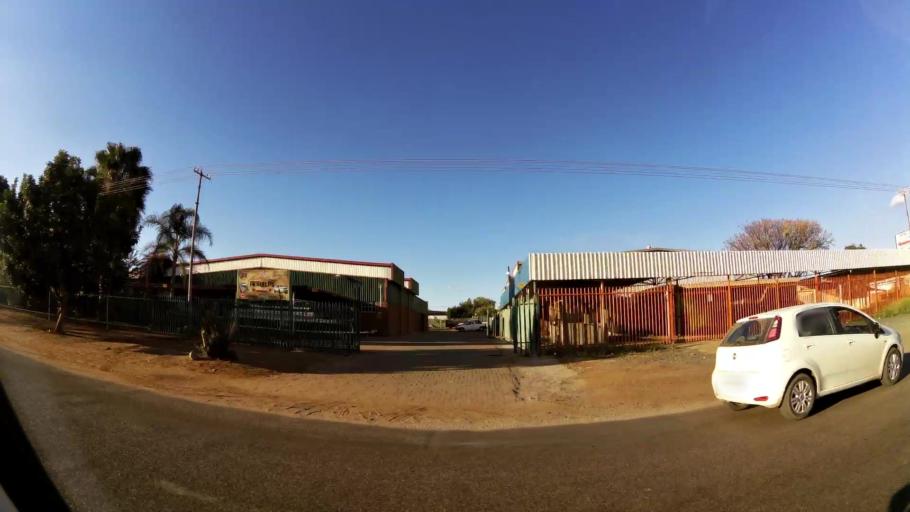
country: ZA
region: Limpopo
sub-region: Waterberg District Municipality
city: Mokopane
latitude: -24.1678
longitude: 28.9961
